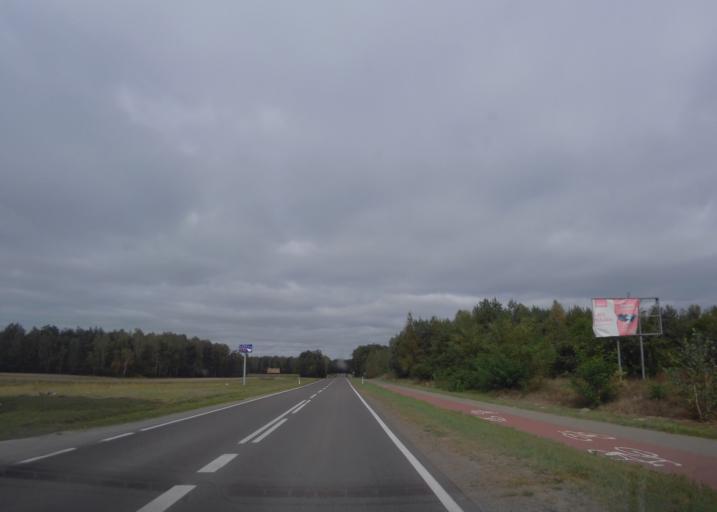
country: PL
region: Lublin Voivodeship
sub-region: Powiat wlodawski
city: Wlodawa
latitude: 51.5124
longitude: 23.5233
